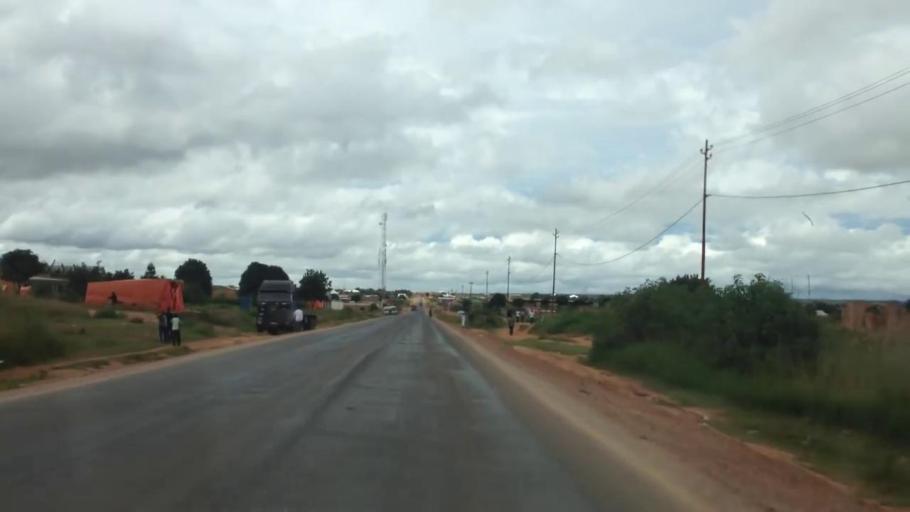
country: CD
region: Katanga
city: Kolwezi
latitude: -10.7308
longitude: 25.5097
